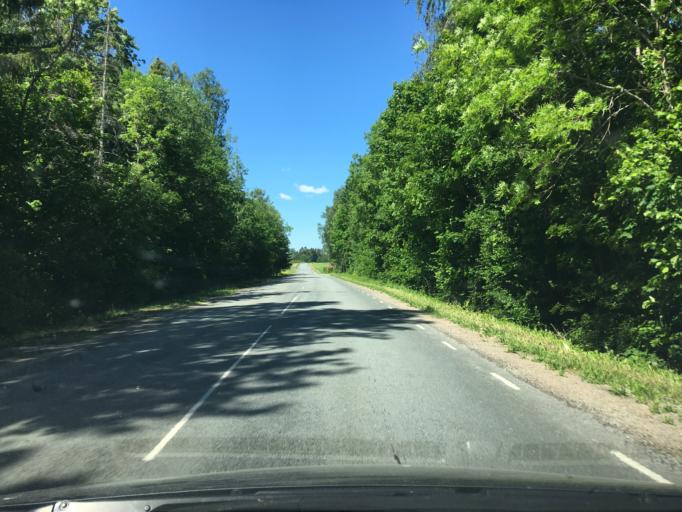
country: EE
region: Harju
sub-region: Rae vald
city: Vaida
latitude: 59.1987
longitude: 24.9664
